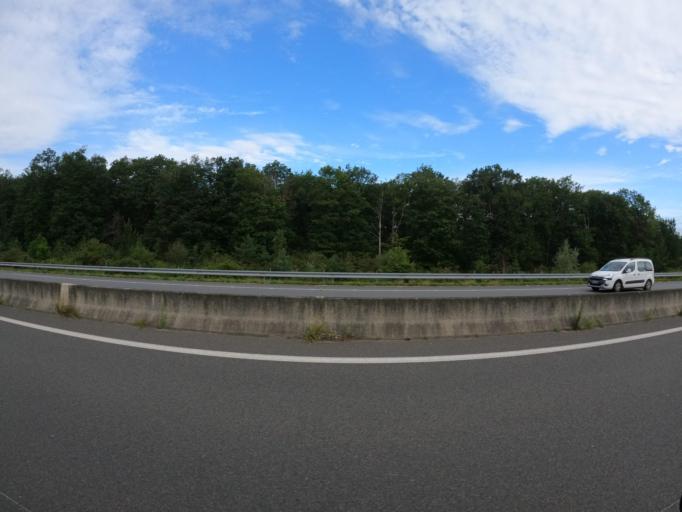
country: FR
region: Centre
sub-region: Departement d'Indre-et-Loire
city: Restigne
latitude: 47.2969
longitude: 0.2888
